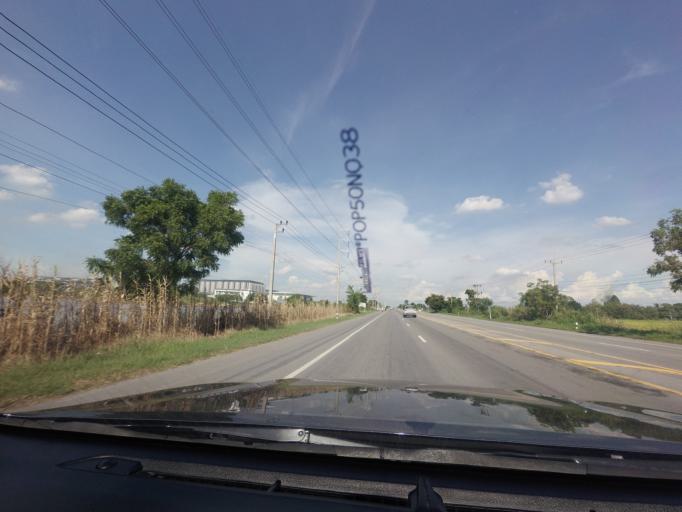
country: TH
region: Phra Nakhon Si Ayutthaya
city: Lat Bua Luang
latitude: 14.1616
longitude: 100.2746
